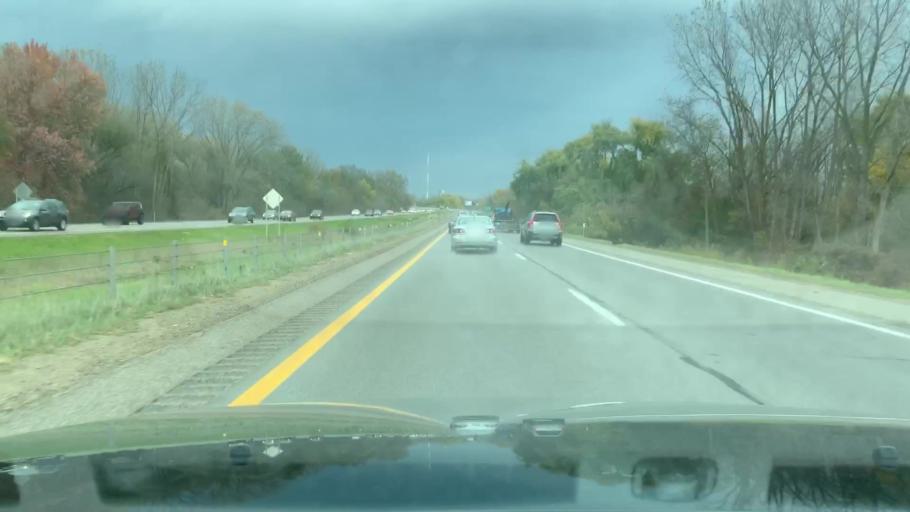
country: US
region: Michigan
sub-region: Kent County
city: Wyoming
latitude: 42.9375
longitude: -85.7189
